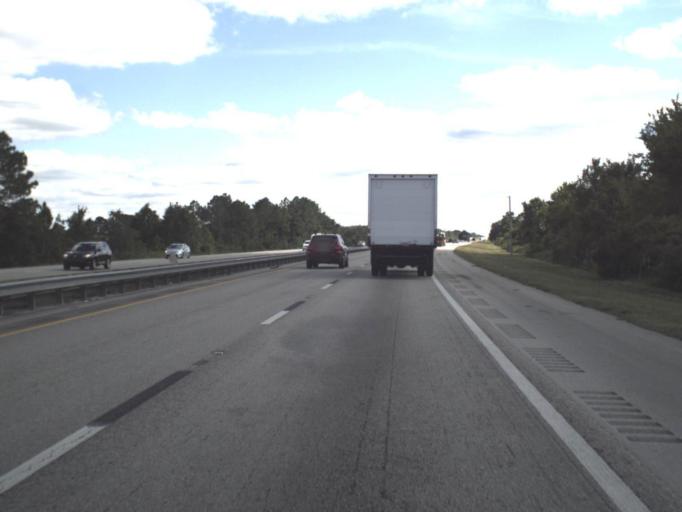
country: US
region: Florida
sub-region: Indian River County
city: Fellsmere
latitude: 27.6560
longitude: -80.8634
